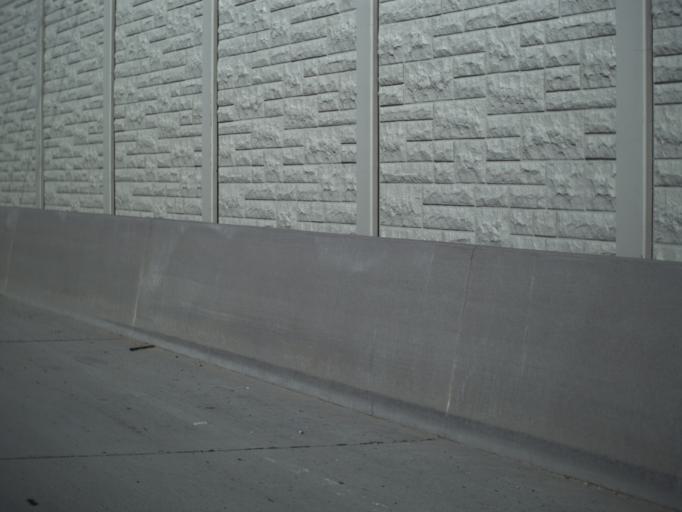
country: US
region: Utah
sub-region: Salt Lake County
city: Draper
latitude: 40.5048
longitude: -111.8905
